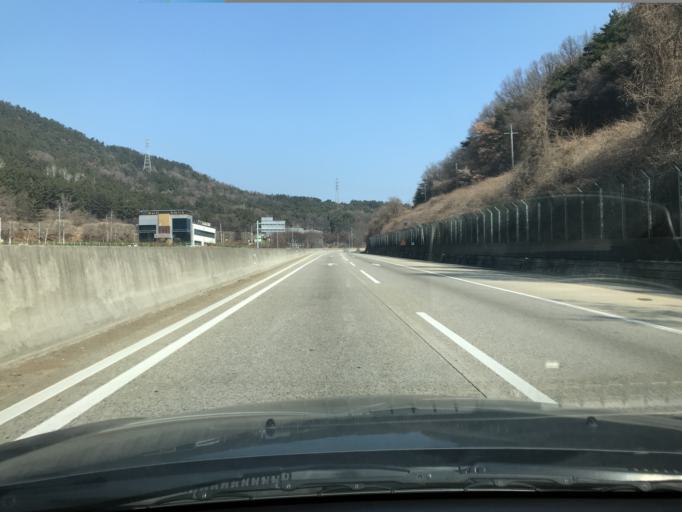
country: KR
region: Daegu
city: Hwawon
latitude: 35.7118
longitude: 128.4436
